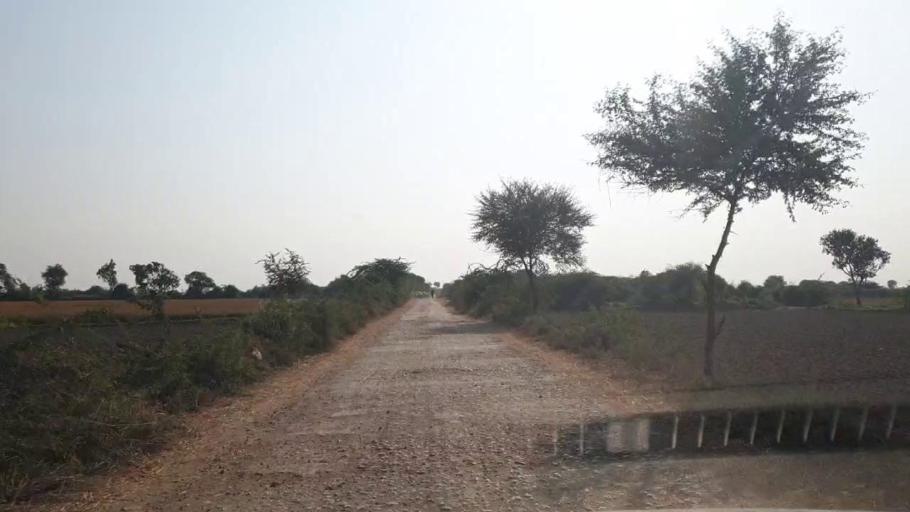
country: PK
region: Sindh
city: Matli
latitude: 24.9493
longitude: 68.6839
